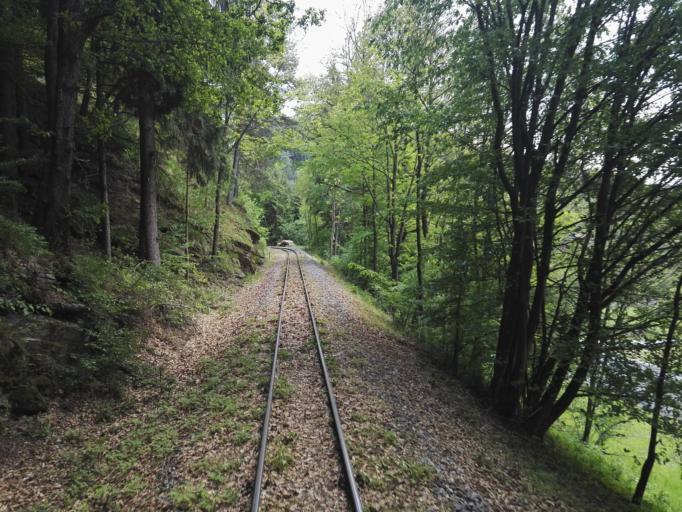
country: AT
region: Styria
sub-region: Politischer Bezirk Weiz
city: Baierdorf-Umgebung
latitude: 47.2581
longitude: 15.7173
